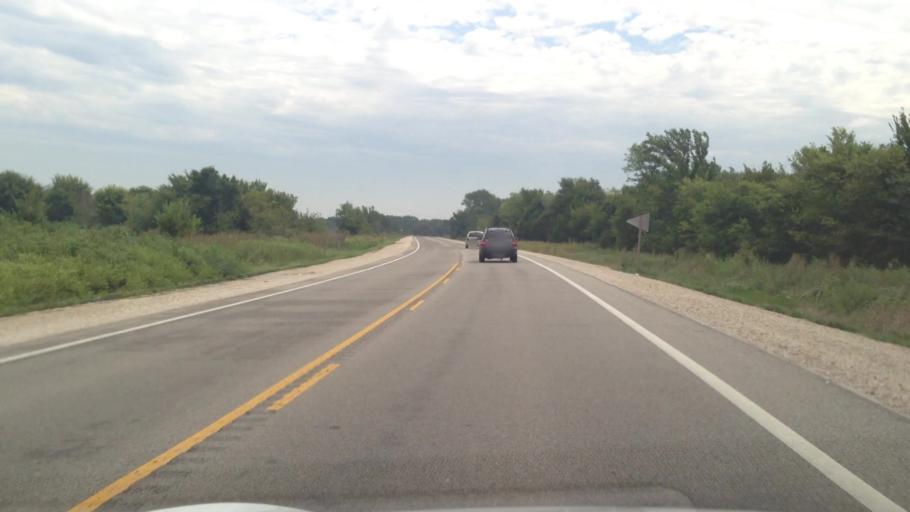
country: US
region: Kansas
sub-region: Allen County
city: Iola
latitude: 37.9145
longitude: -95.1476
